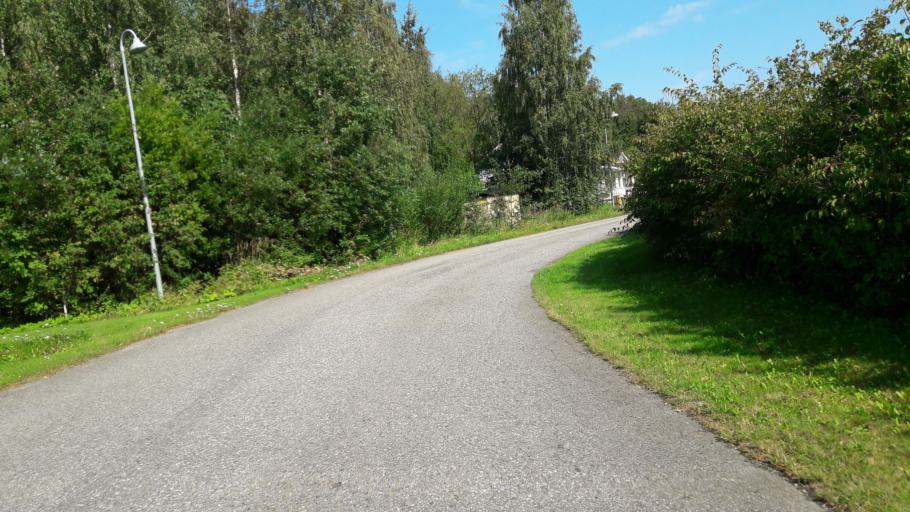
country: FI
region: North Karelia
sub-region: Joensuu
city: Joensuu
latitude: 62.5293
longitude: 29.8415
